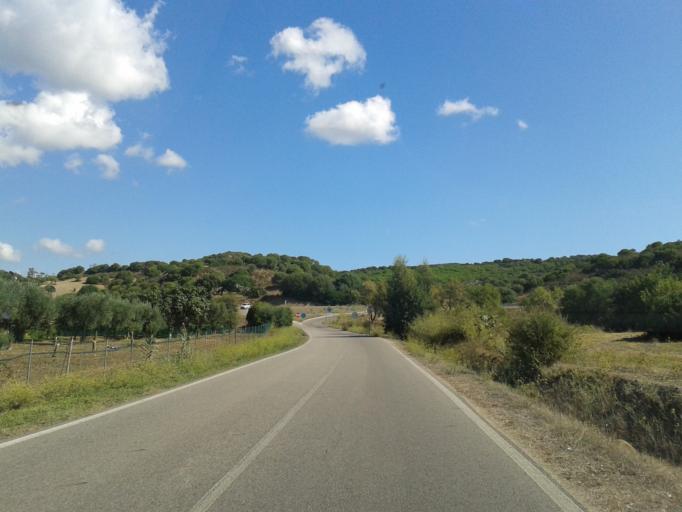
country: IT
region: Sardinia
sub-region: Provincia di Cagliari
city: Villasimius
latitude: 39.1522
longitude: 9.5154
